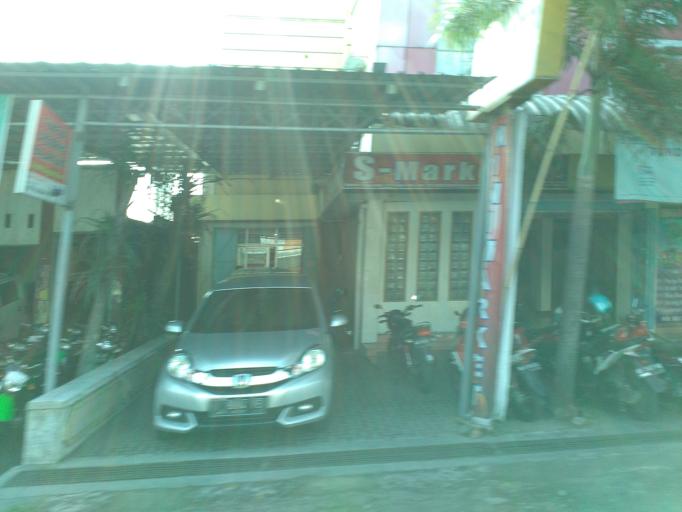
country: ID
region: Central Java
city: Delanggu
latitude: -7.6265
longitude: 110.6962
